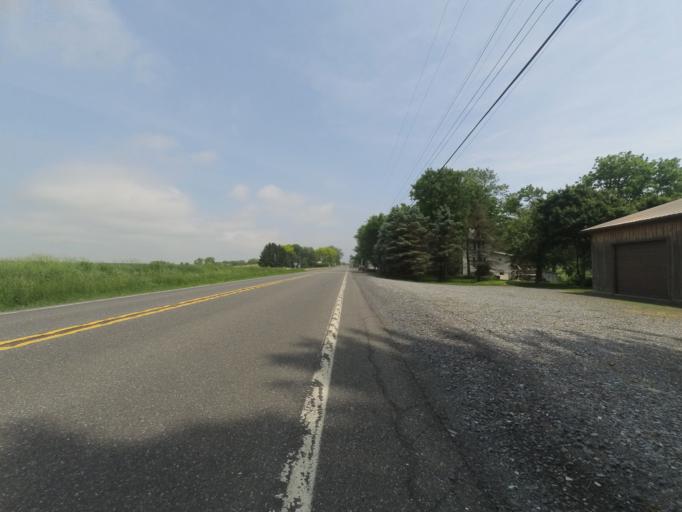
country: US
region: Pennsylvania
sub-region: Centre County
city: Pine Grove Mills
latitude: 40.7089
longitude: -77.9677
